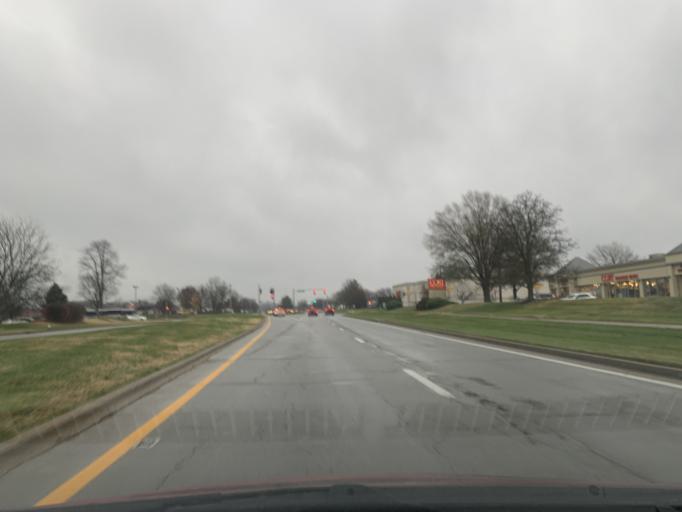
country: US
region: Kentucky
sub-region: Jefferson County
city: Hurstbourne Acres
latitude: 38.2101
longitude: -85.5988
